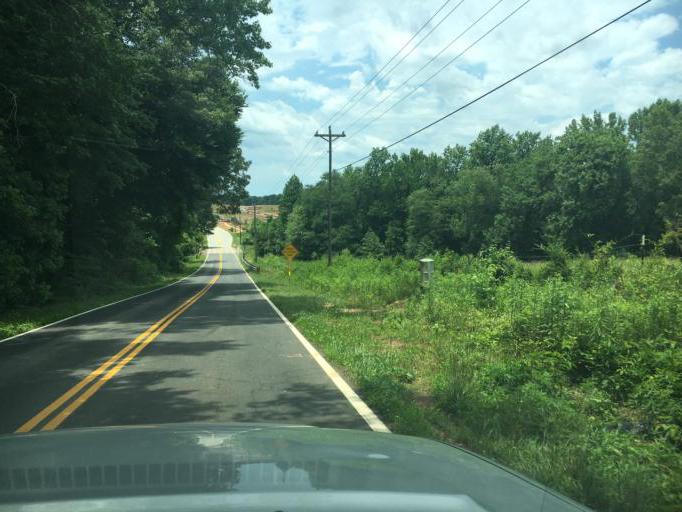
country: US
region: South Carolina
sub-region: Spartanburg County
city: Duncan
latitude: 34.8713
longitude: -82.1587
